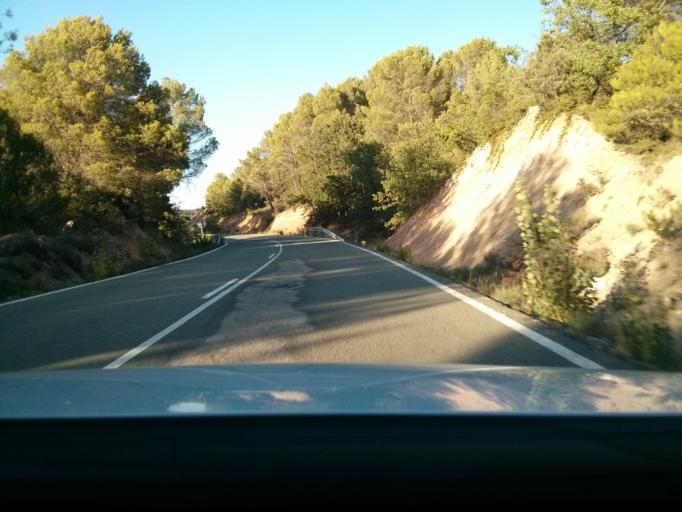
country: ES
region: Castille-La Mancha
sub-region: Provincia de Guadalajara
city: Mantiel
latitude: 40.6235
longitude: -2.6737
